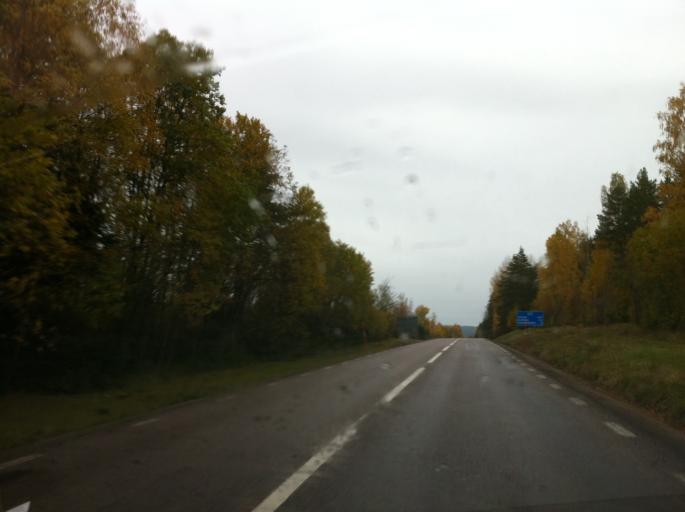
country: SE
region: Dalarna
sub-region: Ludvika Kommun
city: Grangesberg
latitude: 60.2311
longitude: 14.9870
